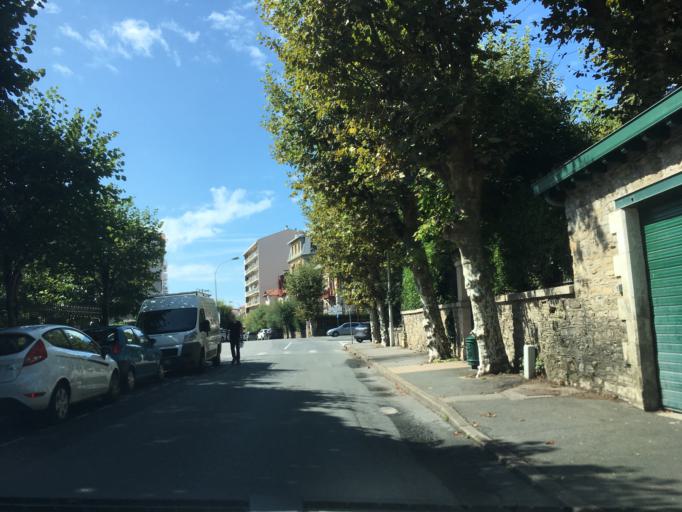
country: FR
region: Aquitaine
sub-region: Departement des Pyrenees-Atlantiques
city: Biarritz
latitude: 43.4852
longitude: -1.5487
